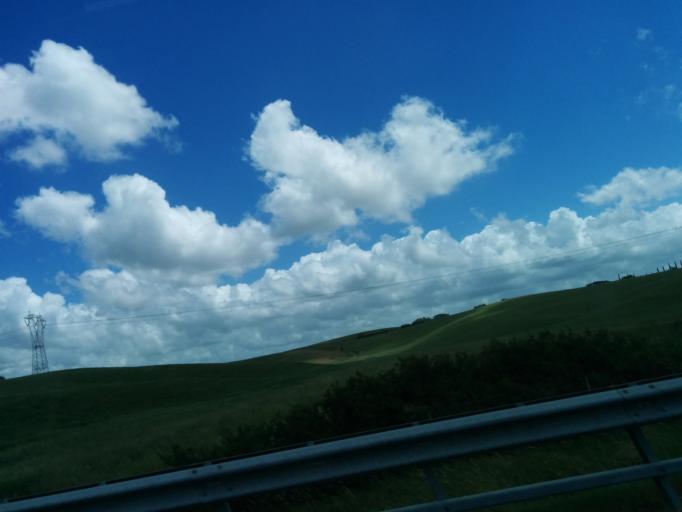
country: IT
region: Tuscany
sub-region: Provincia di Livorno
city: Collesalvetti
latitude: 43.5381
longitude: 10.4661
